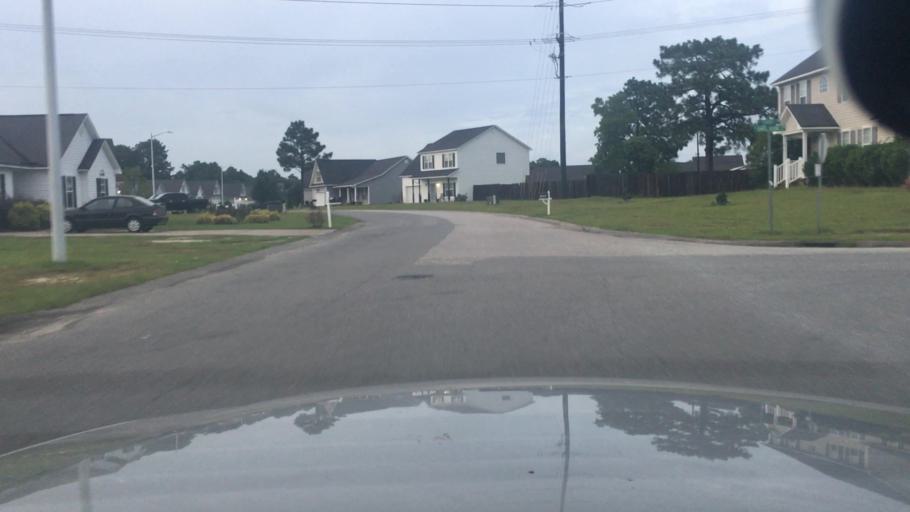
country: US
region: North Carolina
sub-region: Cumberland County
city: Hope Mills
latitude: 34.9849
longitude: -78.9154
